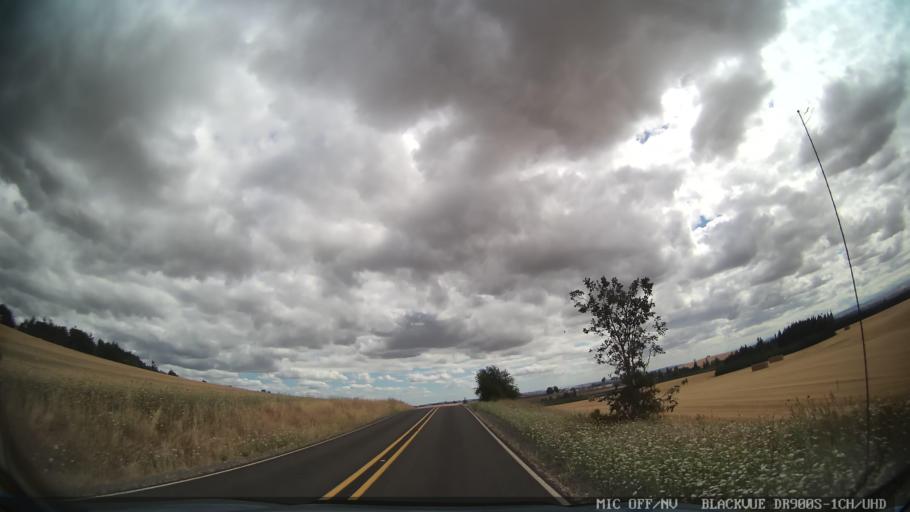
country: US
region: Oregon
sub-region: Marion County
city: Sublimity
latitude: 44.8648
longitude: -122.7386
